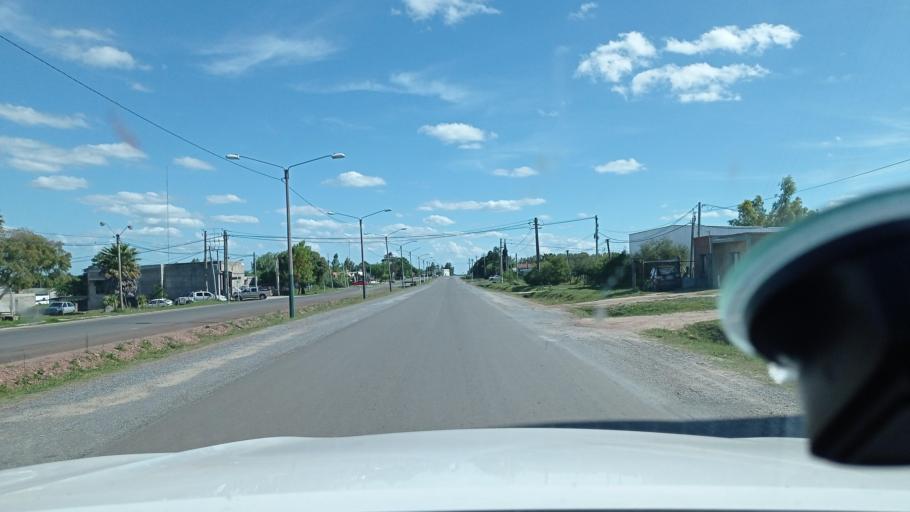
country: UY
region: Florida
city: Florida
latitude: -34.0869
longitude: -56.2376
